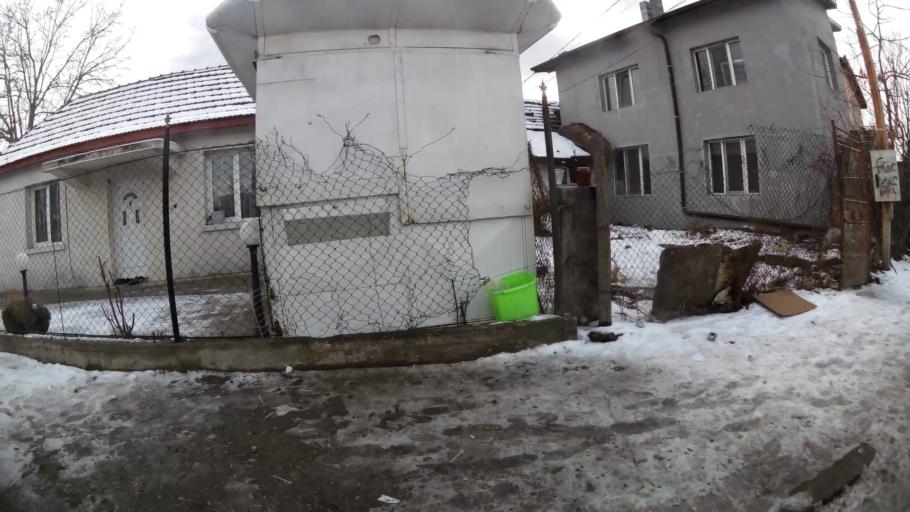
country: BG
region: Sofia-Capital
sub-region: Stolichna Obshtina
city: Sofia
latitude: 42.6880
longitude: 23.3798
